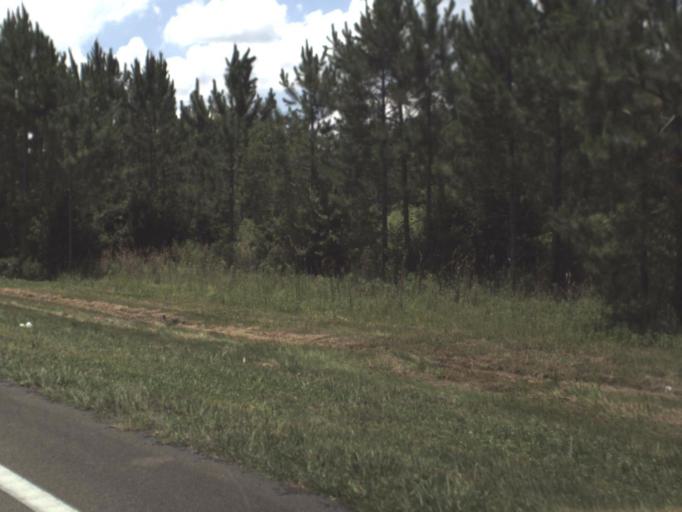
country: US
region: Florida
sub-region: Union County
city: Lake Butler
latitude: 29.9144
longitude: -82.4251
